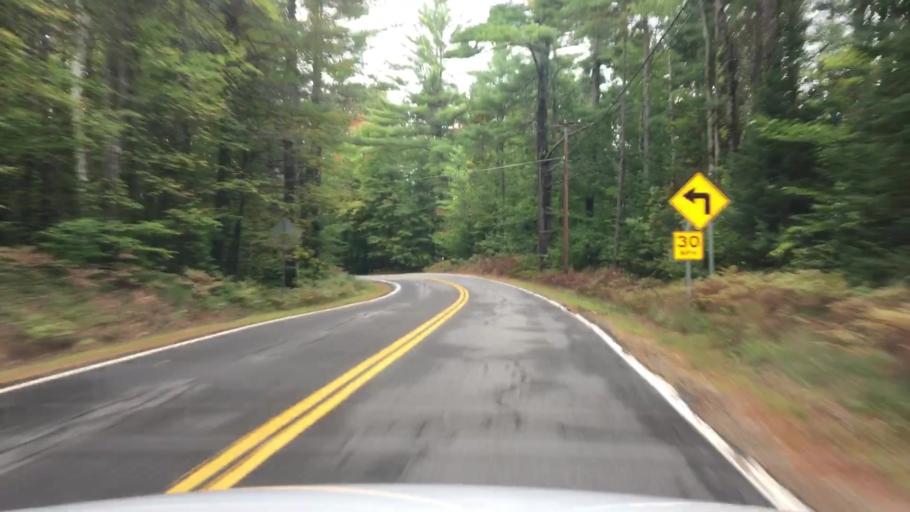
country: US
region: New Hampshire
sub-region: Carroll County
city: Effingham
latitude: 43.7213
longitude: -70.9980
